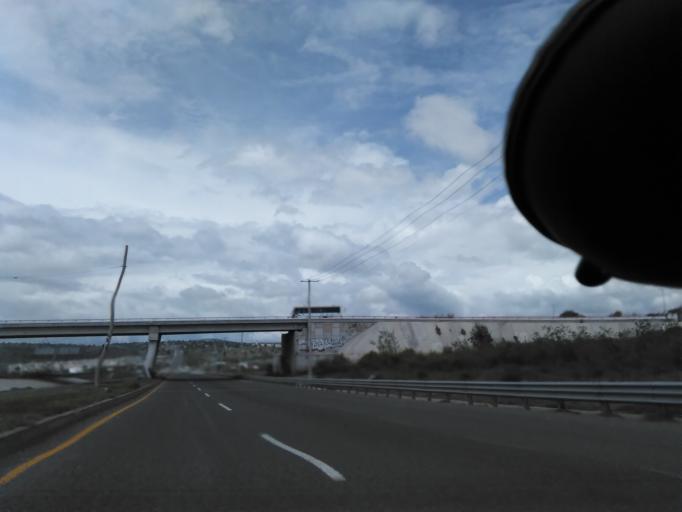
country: MX
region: Hidalgo
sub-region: Atotonilco de Tula
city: Paseos de la Pradera
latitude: 19.9105
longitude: -99.2400
